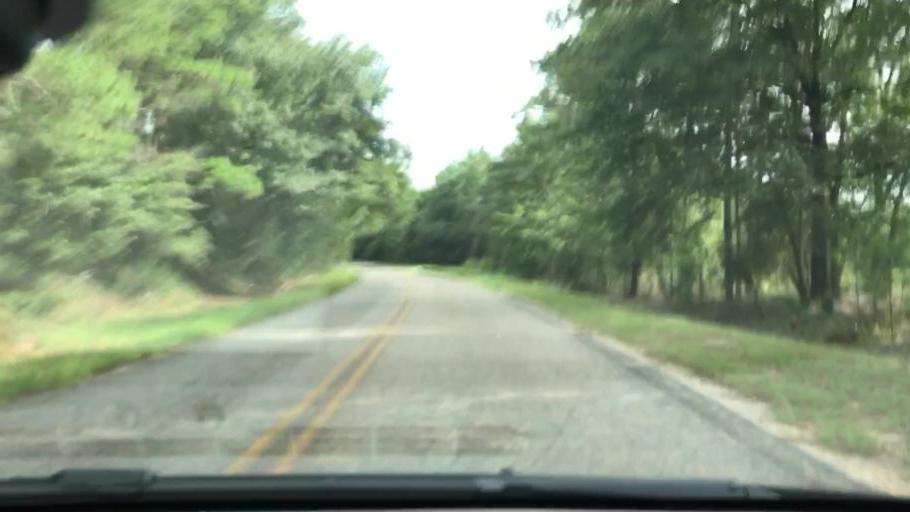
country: US
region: Georgia
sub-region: Early County
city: Blakely
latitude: 31.5100
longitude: -84.9517
